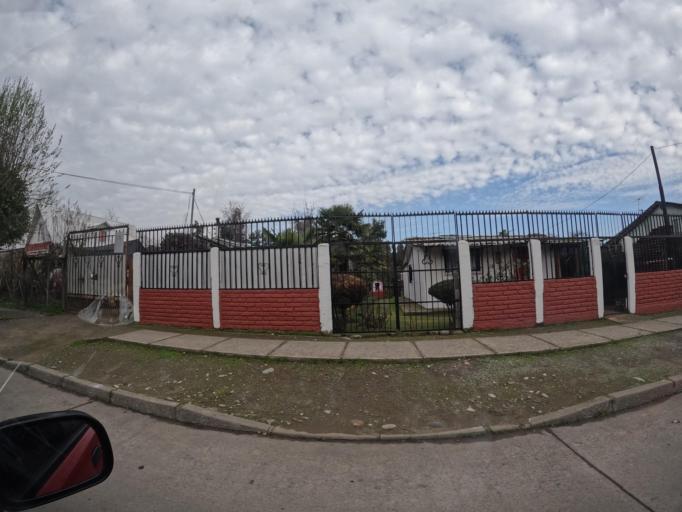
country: CL
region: Maule
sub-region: Provincia de Linares
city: Linares
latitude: -35.8569
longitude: -71.5835
